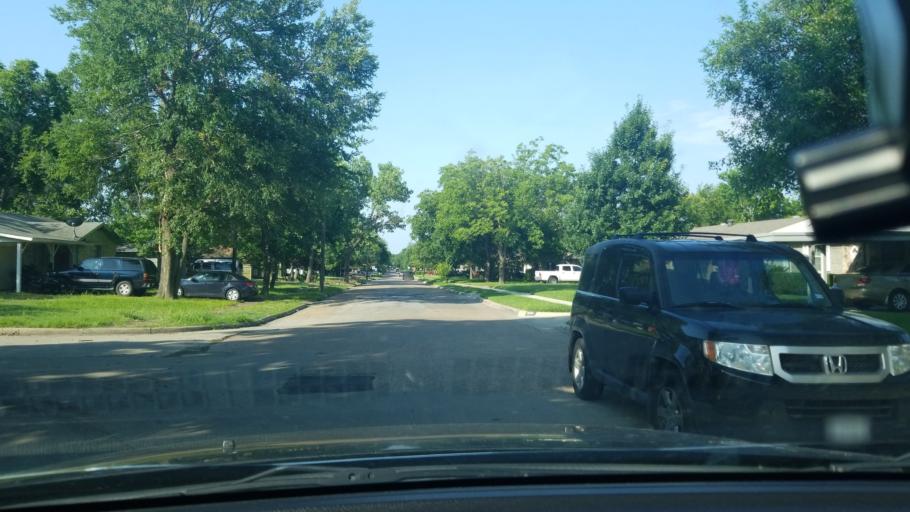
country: US
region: Texas
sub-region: Dallas County
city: Mesquite
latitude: 32.8257
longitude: -96.6354
